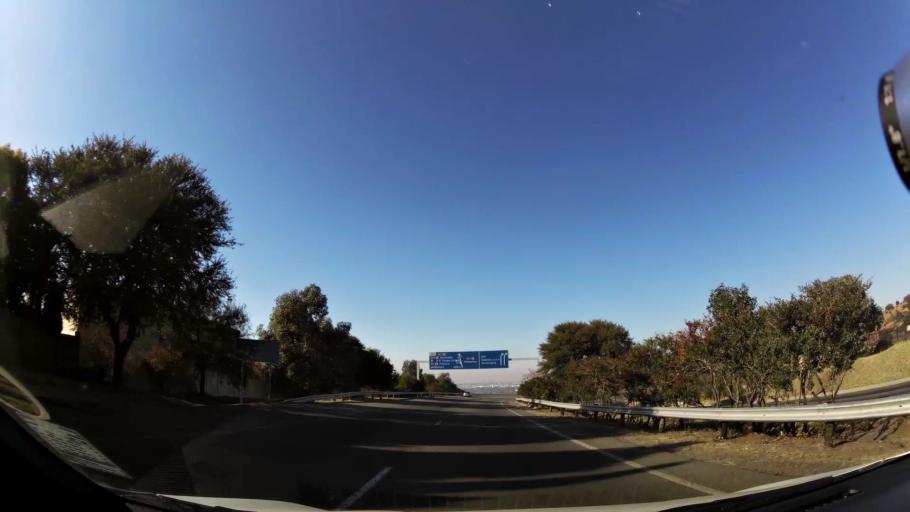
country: ZA
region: Gauteng
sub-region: City of Johannesburg Metropolitan Municipality
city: Johannesburg
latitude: -26.2548
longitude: 28.0992
